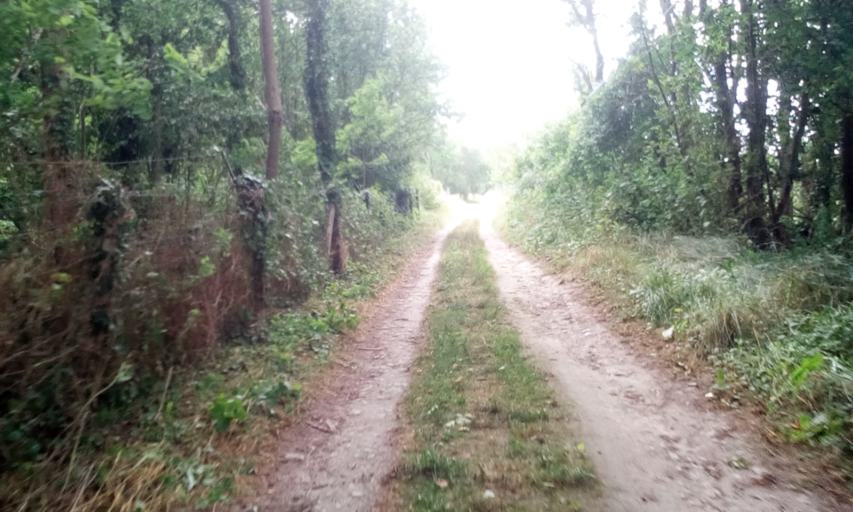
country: FR
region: Lower Normandy
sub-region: Departement du Calvados
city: Creully
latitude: 49.2858
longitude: -0.5221
